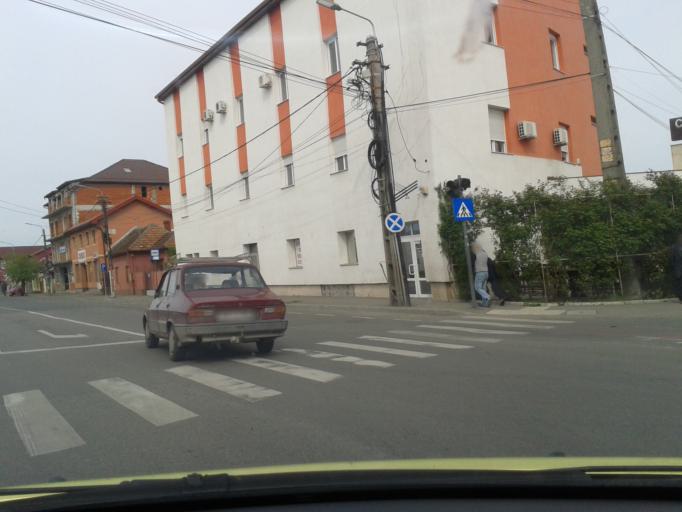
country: RO
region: Arad
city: Arad
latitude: 46.1691
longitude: 21.2915
